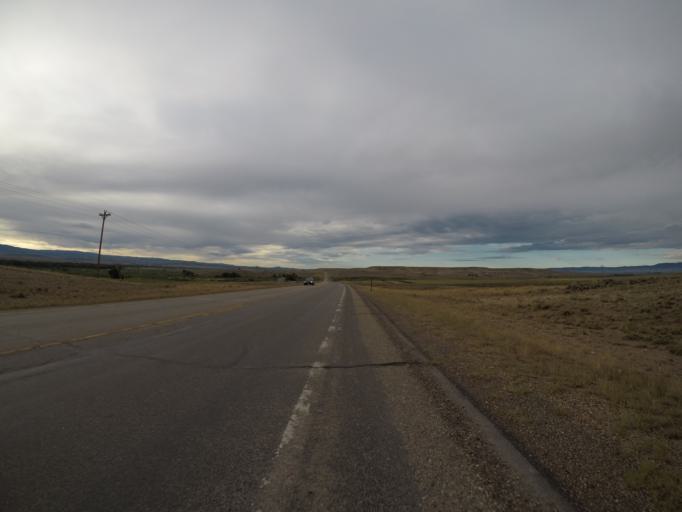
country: US
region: Wyoming
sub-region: Carbon County
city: Saratoga
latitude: 41.4328
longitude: -106.8025
